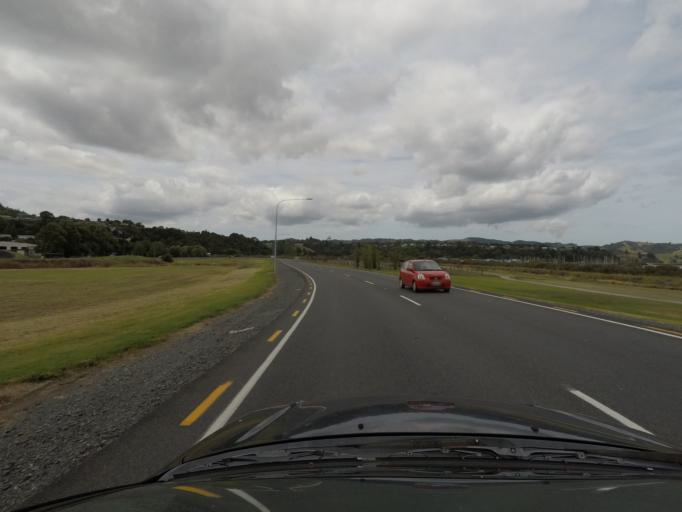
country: NZ
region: Northland
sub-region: Whangarei
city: Whangarei
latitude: -35.7348
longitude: 174.3410
